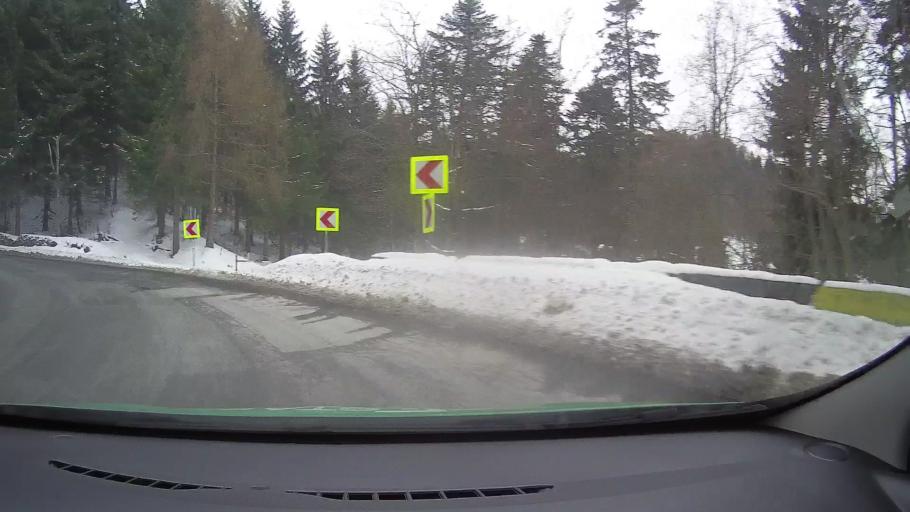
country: RO
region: Brasov
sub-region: Oras Predeal
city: Predeal
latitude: 45.5189
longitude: 25.5002
